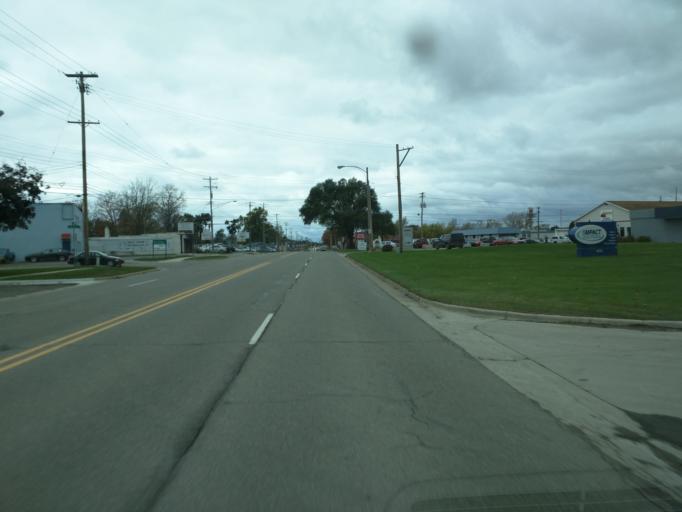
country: US
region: Michigan
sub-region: Ingham County
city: Edgemont Park
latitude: 42.7671
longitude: -84.5918
